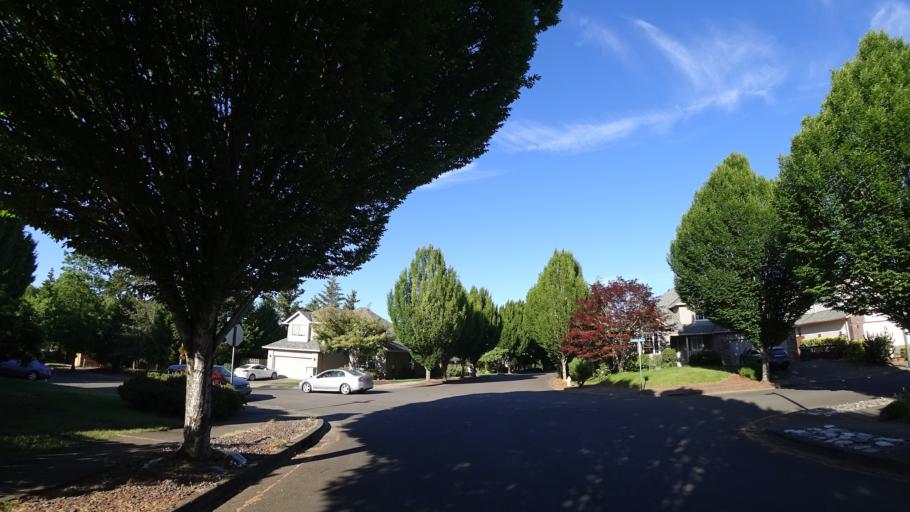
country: US
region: Oregon
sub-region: Washington County
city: Beaverton
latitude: 45.4615
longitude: -122.8118
